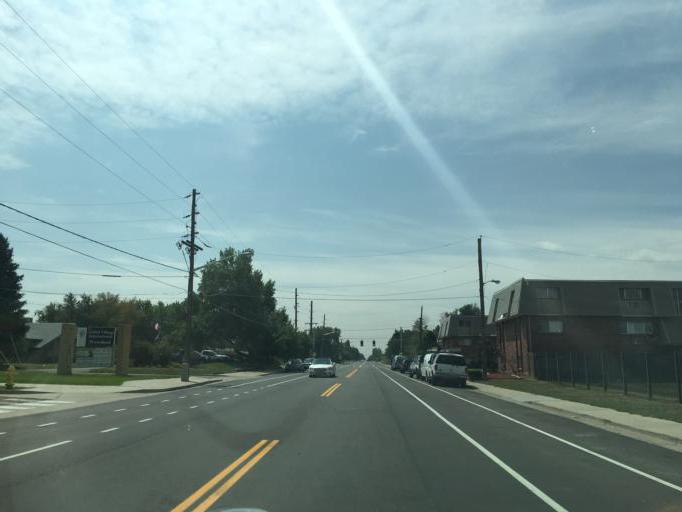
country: US
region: Colorado
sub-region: Adams County
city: Aurora
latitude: 39.7389
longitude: -104.8006
